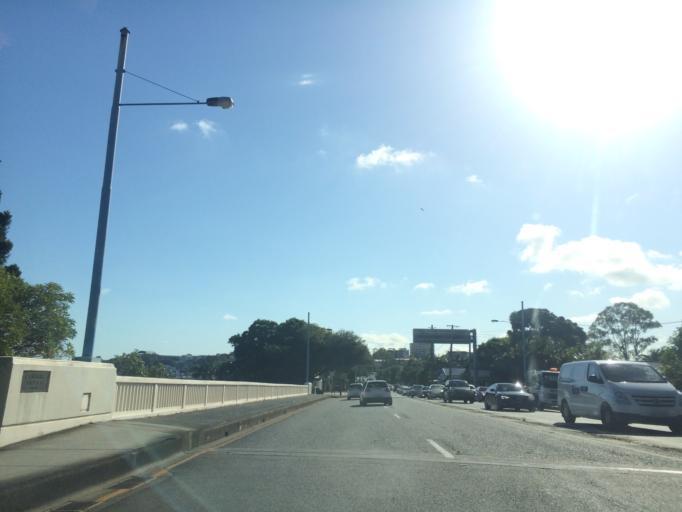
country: AU
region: Queensland
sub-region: Brisbane
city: Woolloongabba
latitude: -27.4766
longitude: 153.0496
